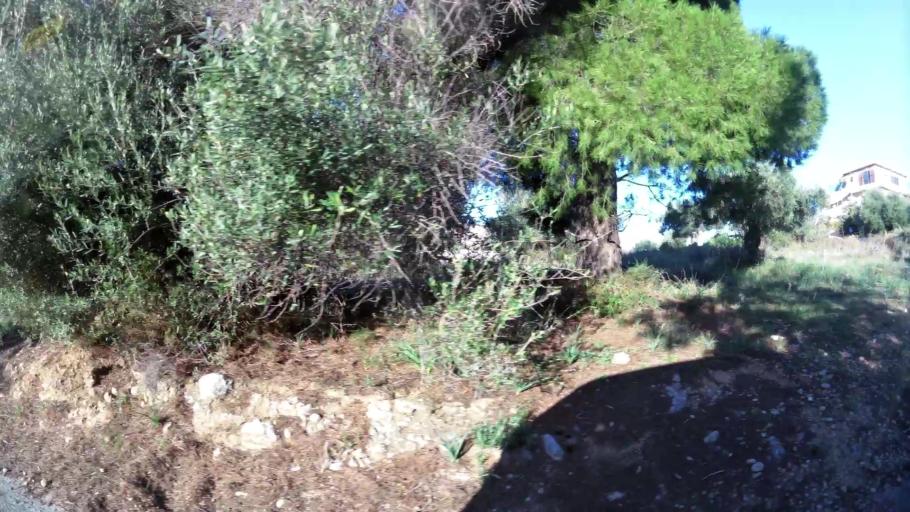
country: GR
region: Attica
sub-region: Nomarchia Anatolikis Attikis
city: Pallini
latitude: 38.0089
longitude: 23.8831
